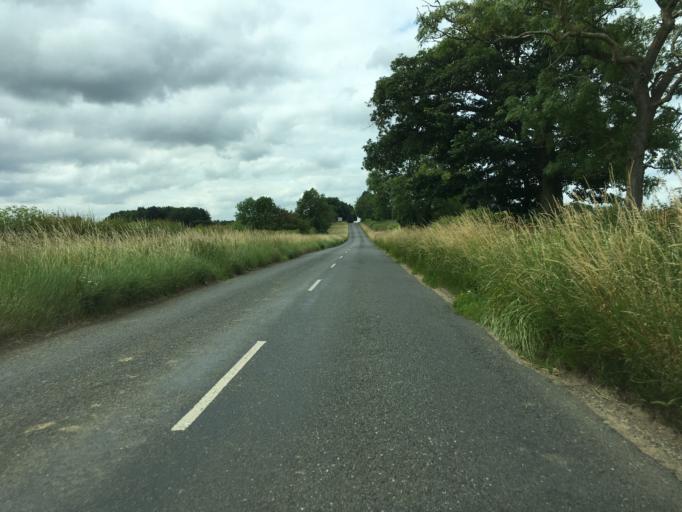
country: GB
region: England
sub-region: Oxfordshire
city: Shipton under Wychwood
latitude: 51.9046
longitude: -1.6043
